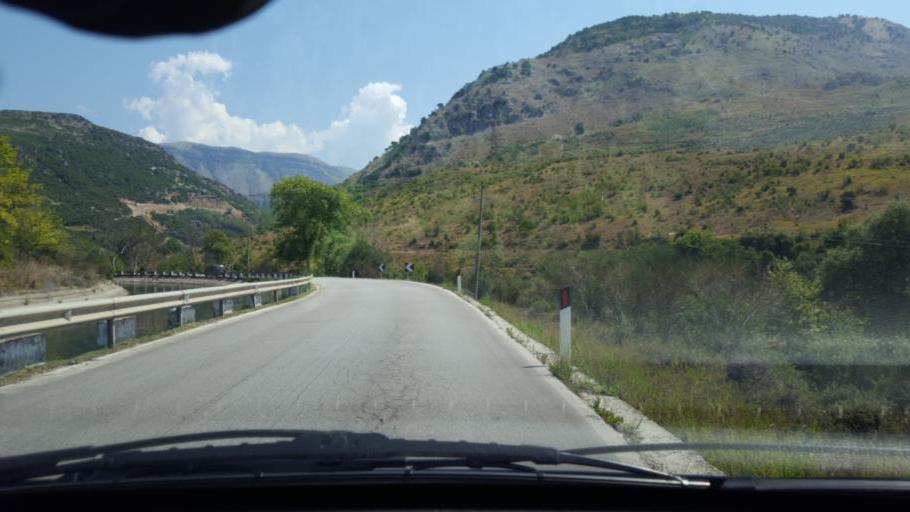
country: AL
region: Vlore
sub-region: Rrethi i Delvines
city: Mesopotam
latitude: 39.9126
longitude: 20.1306
